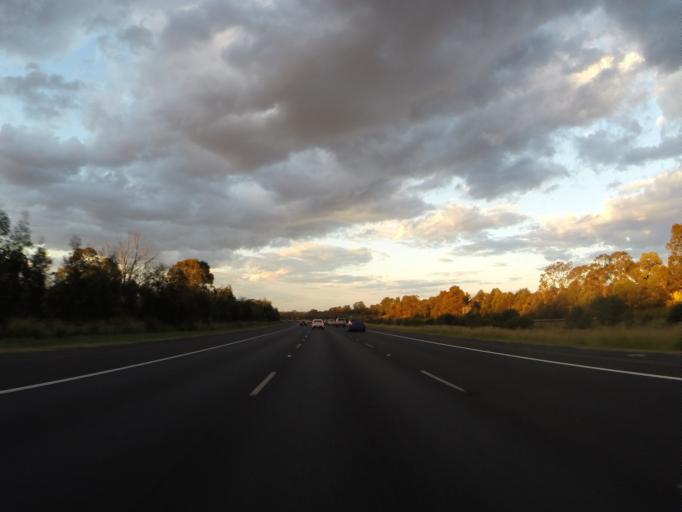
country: AU
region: New South Wales
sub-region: Campbelltown Municipality
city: Campbelltown
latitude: -34.0492
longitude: 150.8151
